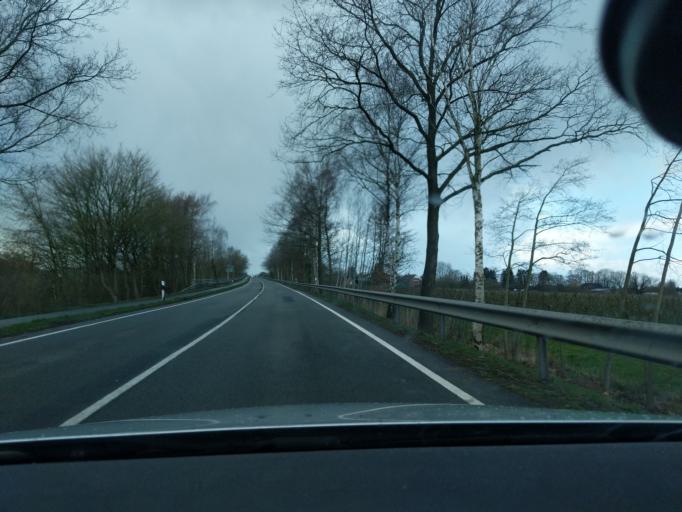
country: DE
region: Lower Saxony
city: Osten
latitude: 53.6982
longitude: 9.1841
